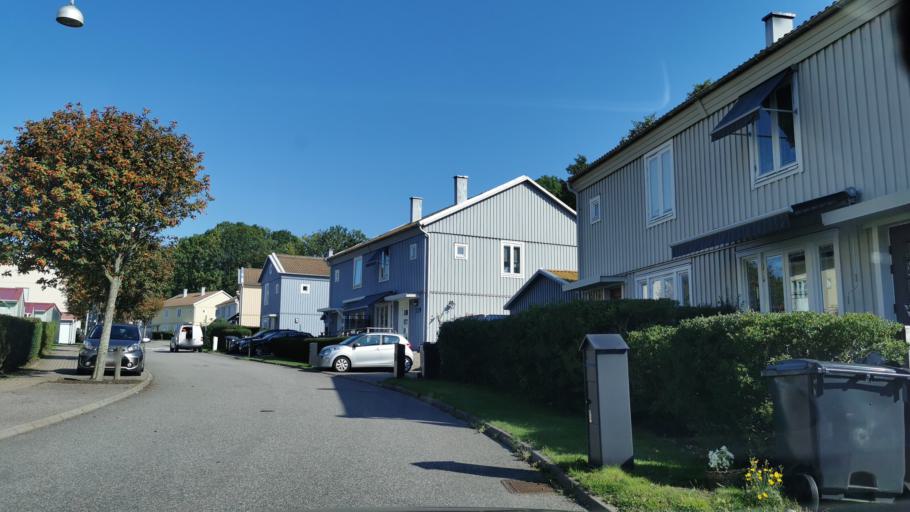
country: SE
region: Vaestra Goetaland
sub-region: Molndal
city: Moelndal
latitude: 57.6556
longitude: 11.9629
